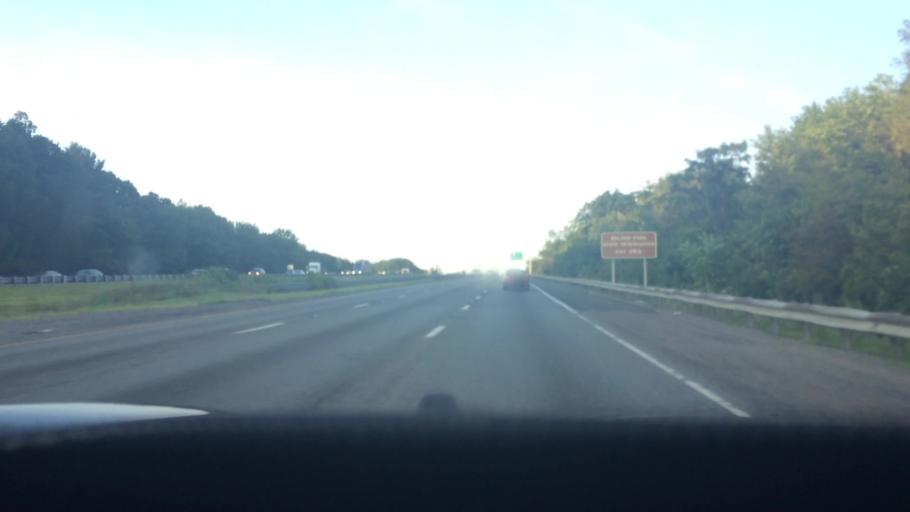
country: US
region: Massachusetts
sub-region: Middlesex County
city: Littleton Common
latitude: 42.5304
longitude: -71.5009
